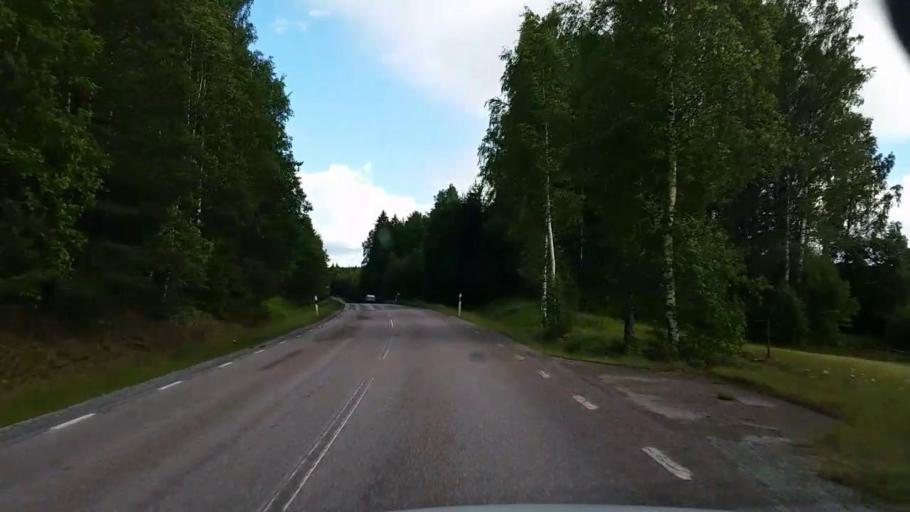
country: SE
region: Vaestmanland
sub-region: Fagersta Kommun
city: Fagersta
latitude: 59.9417
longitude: 15.8050
